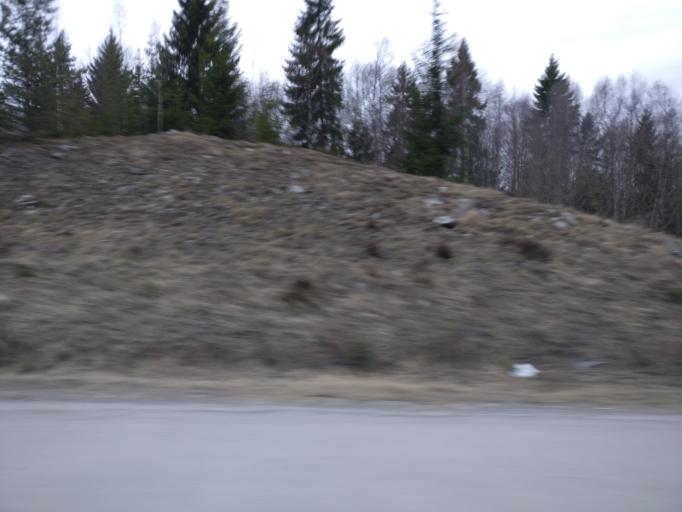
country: FI
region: Uusimaa
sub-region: Helsinki
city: Nurmijaervi
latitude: 60.3786
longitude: 24.8143
